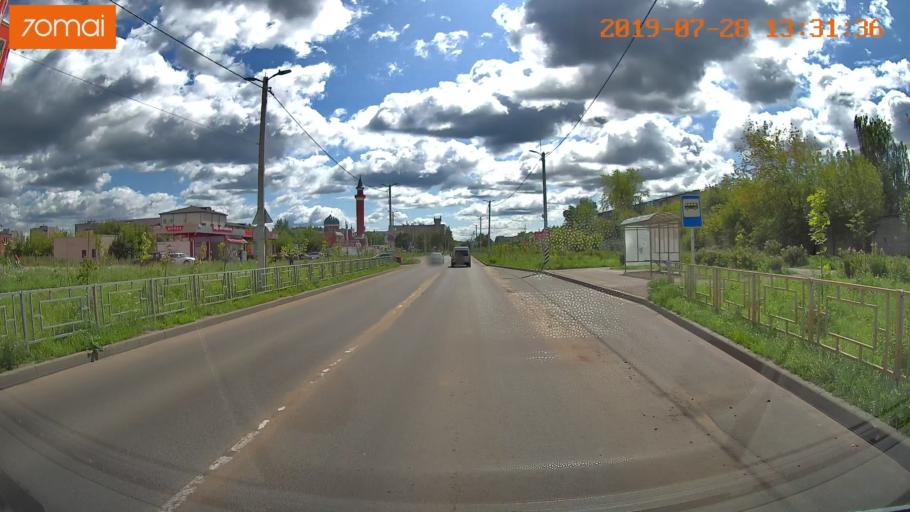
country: RU
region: Ivanovo
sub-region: Gorod Ivanovo
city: Ivanovo
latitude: 56.9665
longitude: 40.9845
